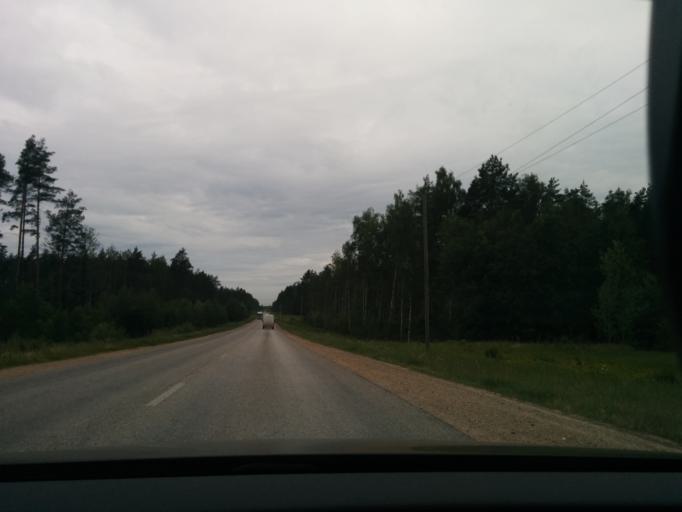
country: LV
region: Stopini
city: Ulbroka
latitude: 56.9150
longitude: 24.3201
